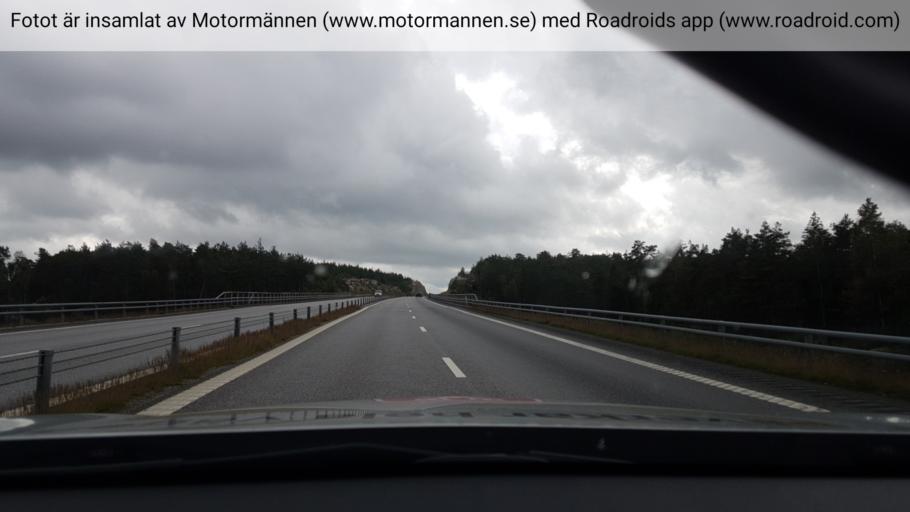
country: SE
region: Vaestra Goetaland
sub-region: Stromstads Kommun
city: Stroemstad
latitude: 58.9041
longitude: 11.2711
